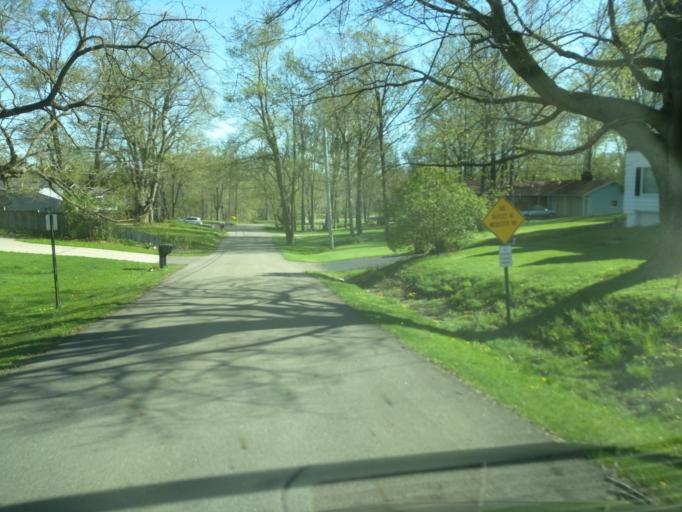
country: US
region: Michigan
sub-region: Eaton County
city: Waverly
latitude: 42.7646
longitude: -84.6475
